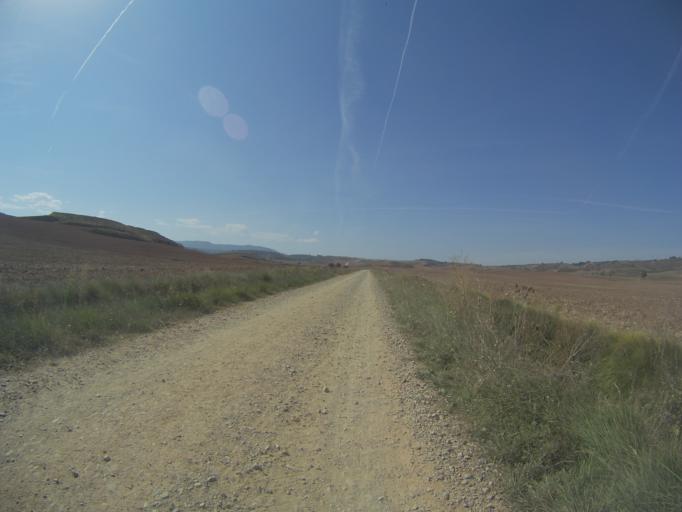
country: ES
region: La Rioja
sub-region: Provincia de La Rioja
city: Torrecilla sobre Alesanco
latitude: 42.4318
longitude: -2.8508
